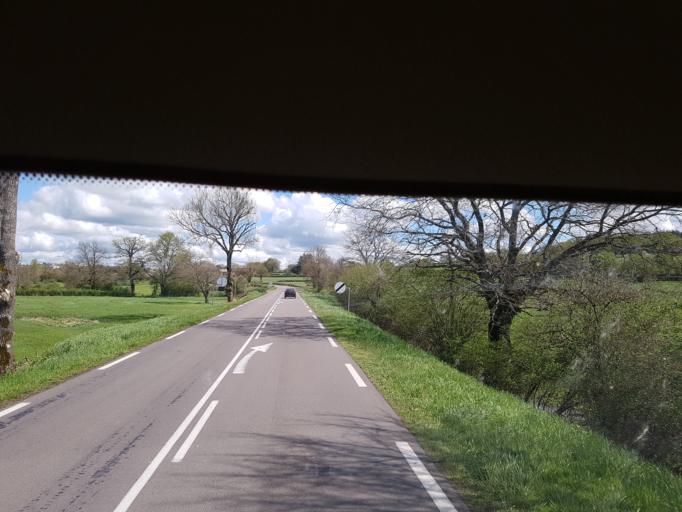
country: FR
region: Bourgogne
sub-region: Departement de Saone-et-Loire
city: Charolles
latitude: 46.4188
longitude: 4.2548
